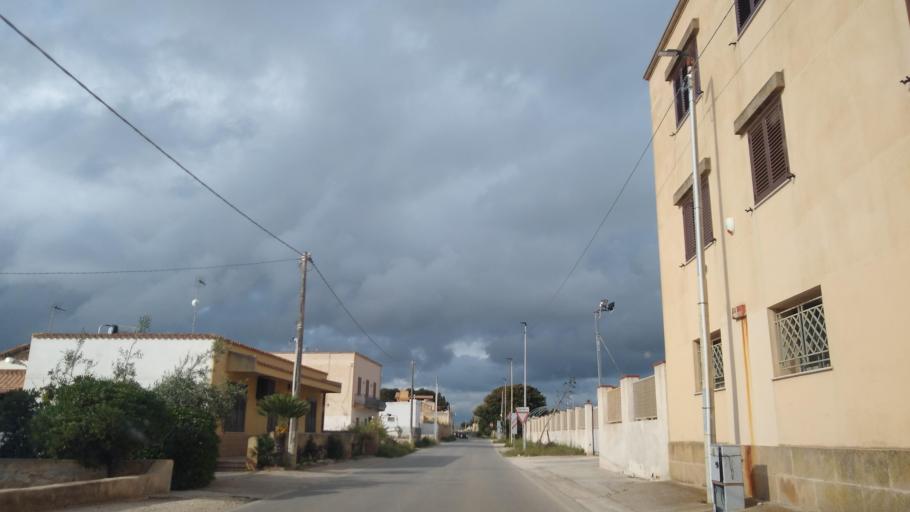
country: IT
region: Sicily
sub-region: Trapani
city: Marsala
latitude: 37.8544
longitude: 12.4862
